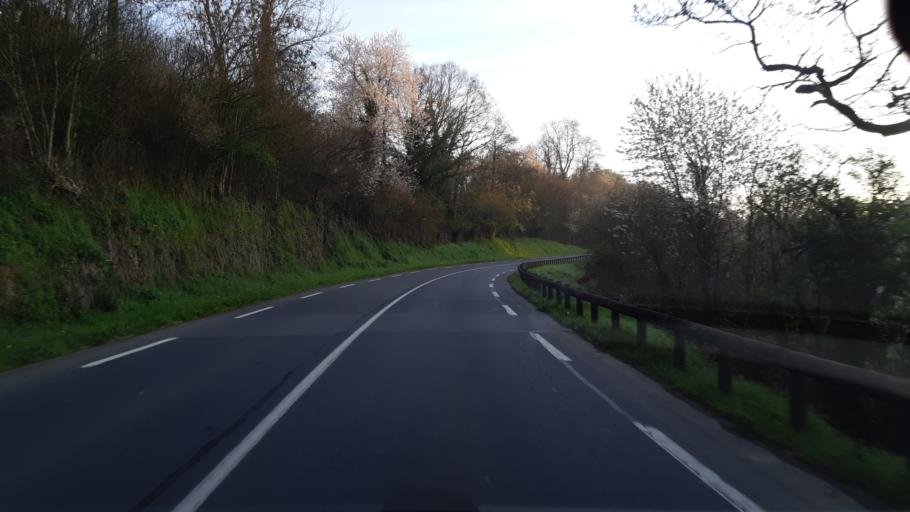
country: FR
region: Lower Normandy
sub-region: Departement de la Manche
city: Agneaux
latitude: 49.0739
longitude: -1.1275
